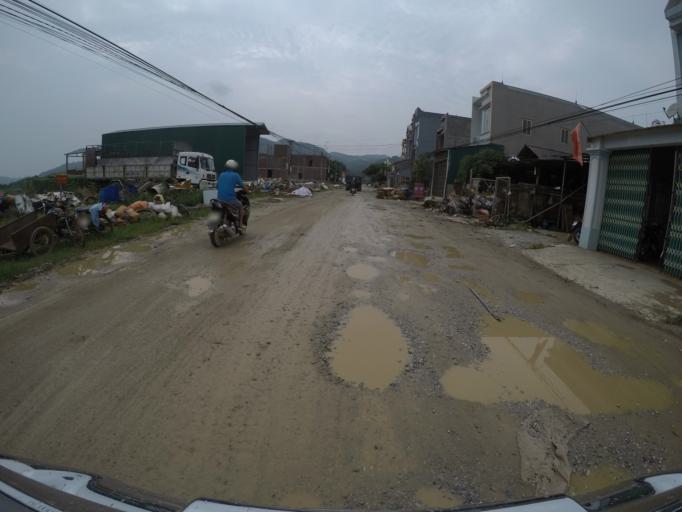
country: VN
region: Yen Bai
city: Co Phuc
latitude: 21.8655
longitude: 104.6426
